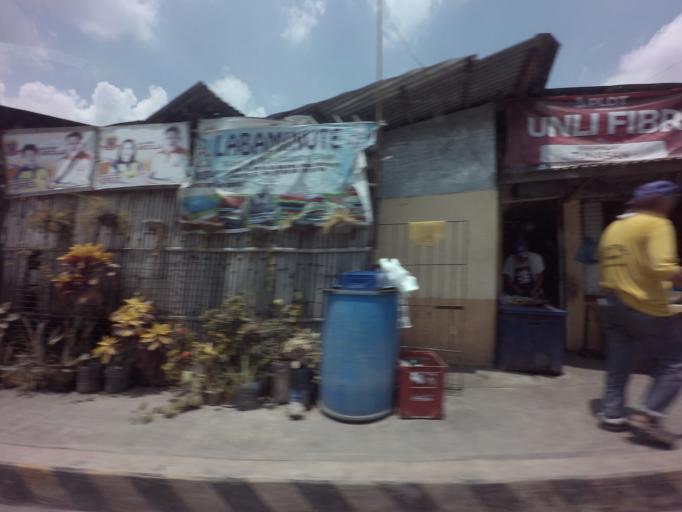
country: PH
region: Calabarzon
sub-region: Province of Laguna
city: San Pedro
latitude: 14.3862
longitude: 121.0503
